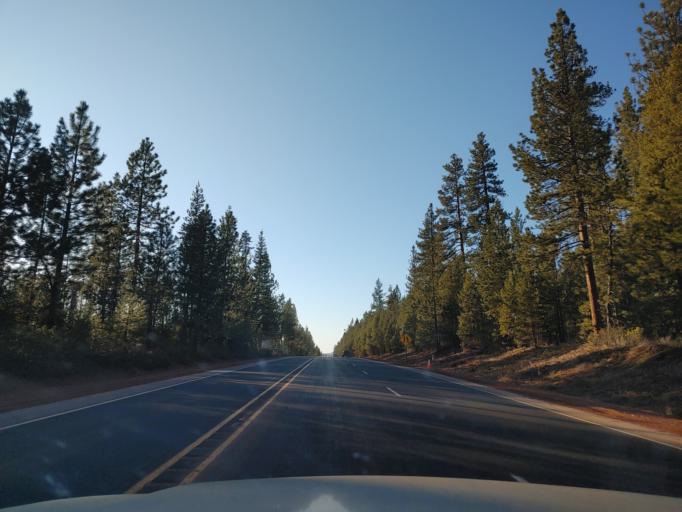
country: US
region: Oregon
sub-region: Deschutes County
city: La Pine
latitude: 43.4557
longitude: -121.8760
